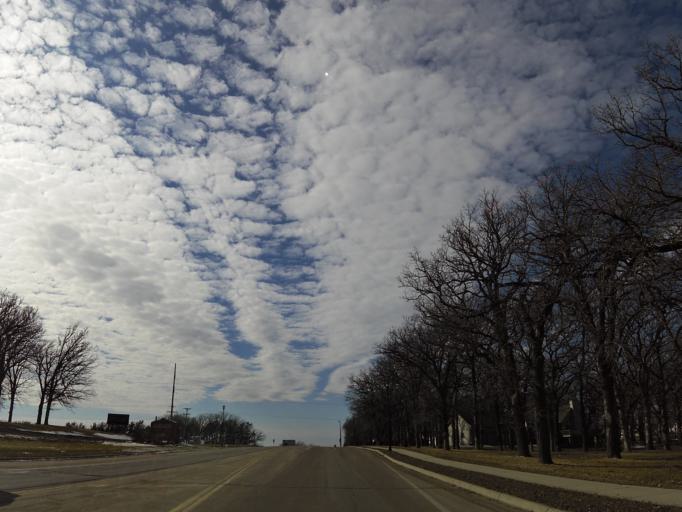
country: US
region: Minnesota
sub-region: Waseca County
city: Waseca
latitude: 44.0789
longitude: -93.5249
